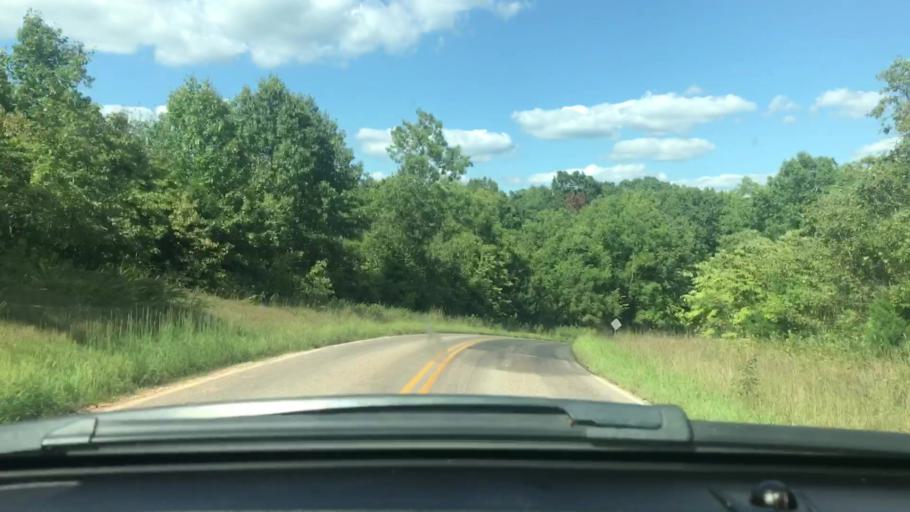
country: US
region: Missouri
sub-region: Wright County
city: Hartville
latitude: 37.3778
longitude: -92.3703
